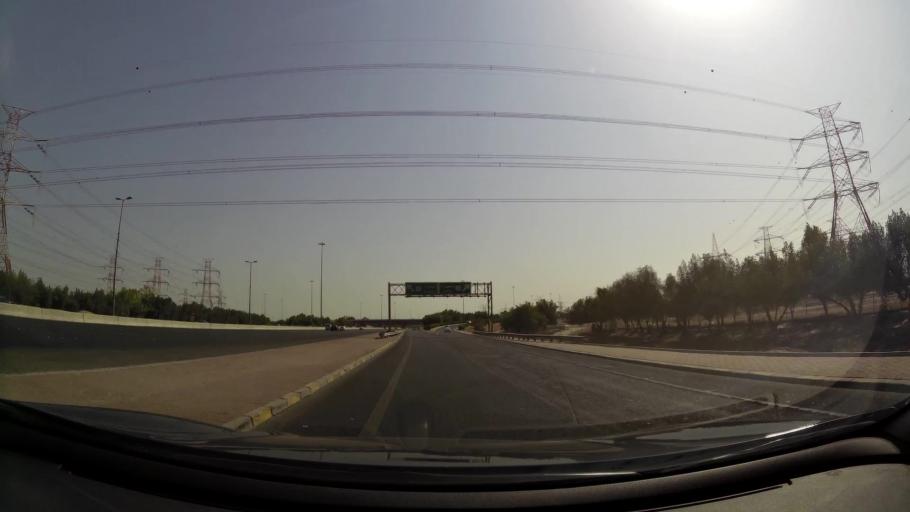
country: KW
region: Mubarak al Kabir
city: Sabah as Salim
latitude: 29.2702
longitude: 48.0396
